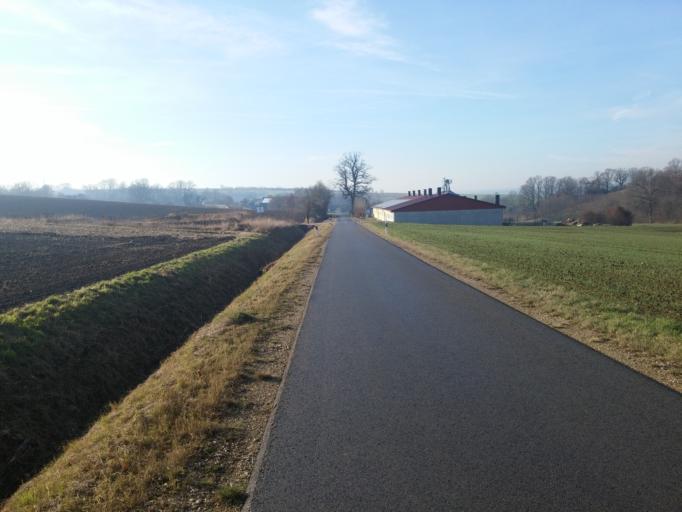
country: DE
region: Bavaria
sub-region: Upper Franconia
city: Untersiemau
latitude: 50.1717
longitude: 10.9711
